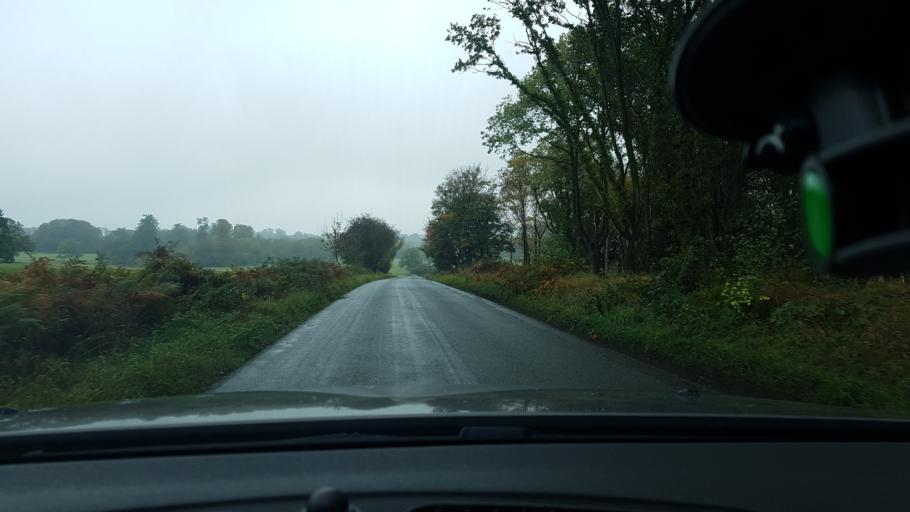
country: GB
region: England
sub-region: Wiltshire
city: Burbage
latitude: 51.3822
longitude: -1.6519
